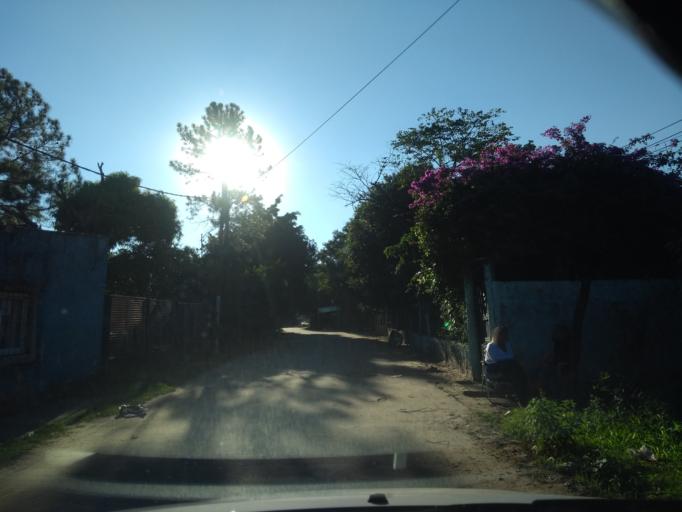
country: AR
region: Chaco
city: Barranqueras
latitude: -27.4815
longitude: -58.9221
